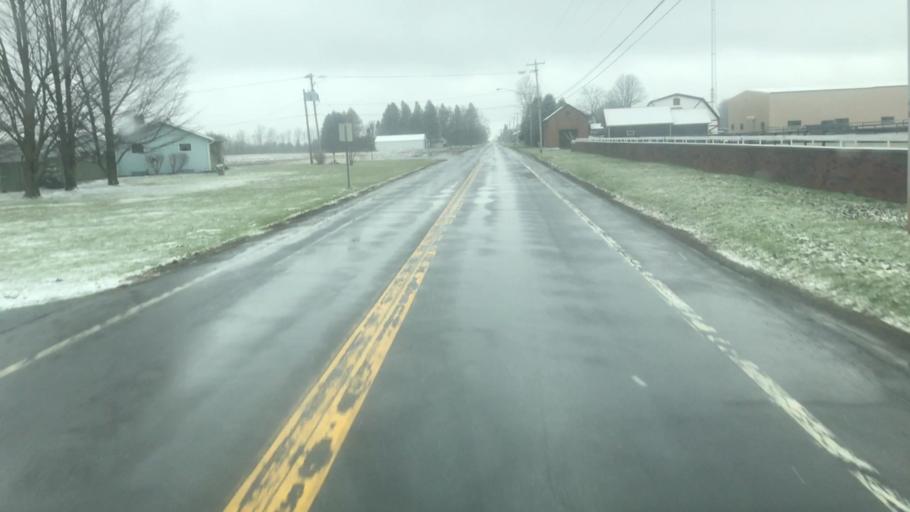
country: US
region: New York
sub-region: Onondaga County
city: Marcellus
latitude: 42.9950
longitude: -76.3869
